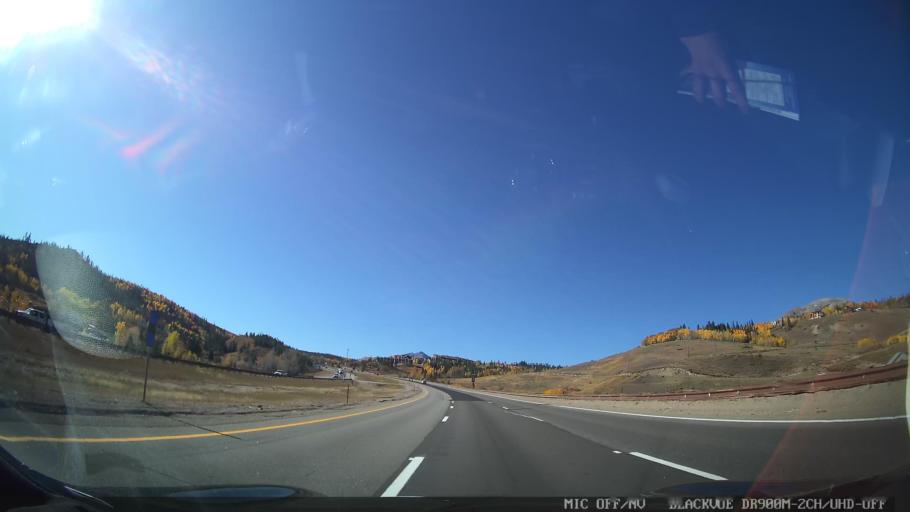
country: US
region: Colorado
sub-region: Summit County
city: Silverthorne
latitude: 39.6261
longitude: -106.0719
